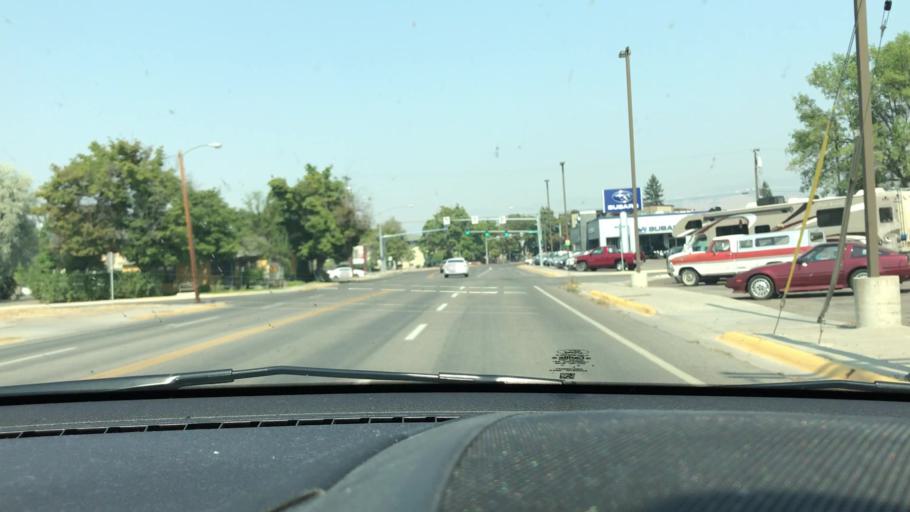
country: US
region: Montana
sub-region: Missoula County
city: Missoula
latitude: 46.8546
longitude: -114.0127
